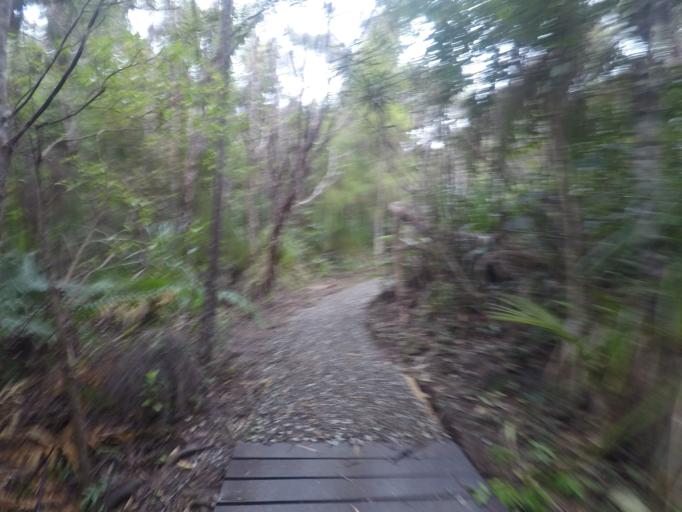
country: NZ
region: Auckland
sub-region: Auckland
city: Titirangi
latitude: -37.0009
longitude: 174.5397
